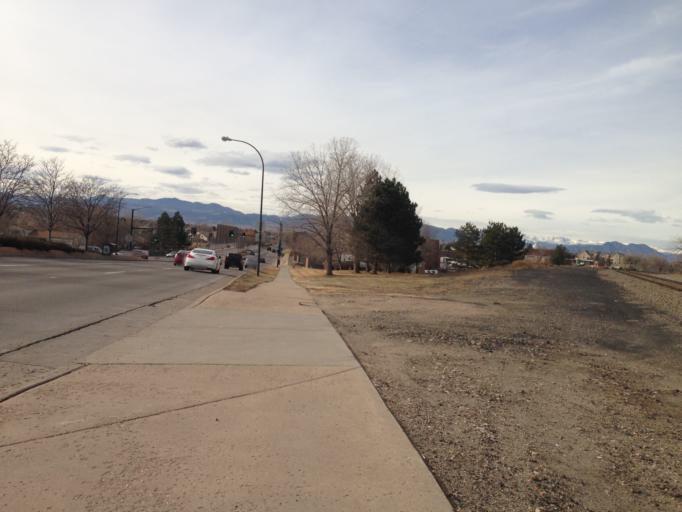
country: US
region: Colorado
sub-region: Adams County
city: Westminster
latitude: 39.8567
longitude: -105.0651
